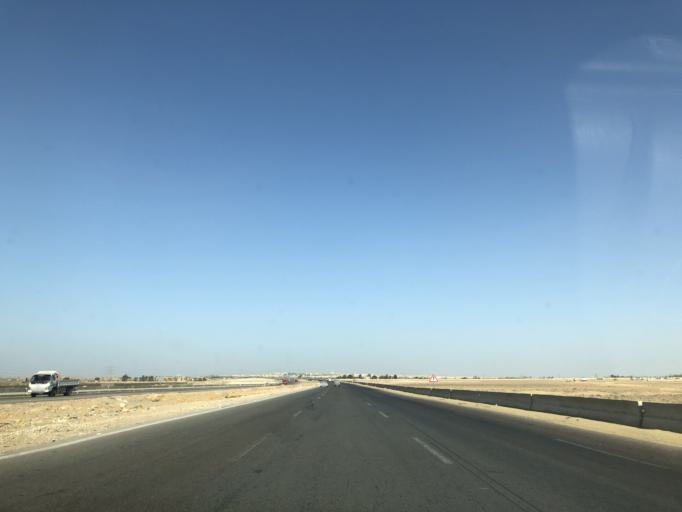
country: EG
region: Muhafazat al Minufiyah
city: Ashmun
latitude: 30.0678
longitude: 30.8954
